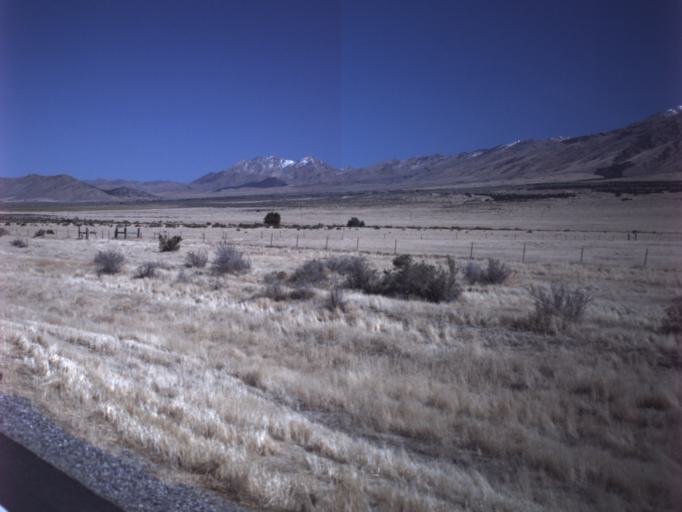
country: US
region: Utah
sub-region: Tooele County
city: Grantsville
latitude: 40.4657
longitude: -112.7469
